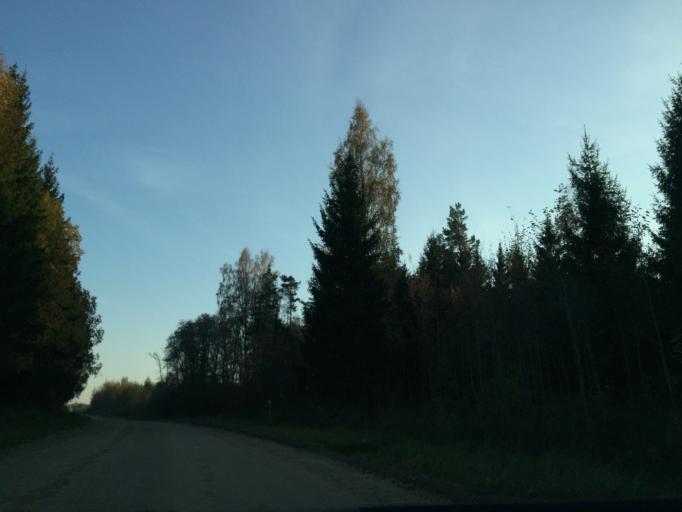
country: LV
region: Vainode
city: Vainode
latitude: 56.5742
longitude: 21.8446
